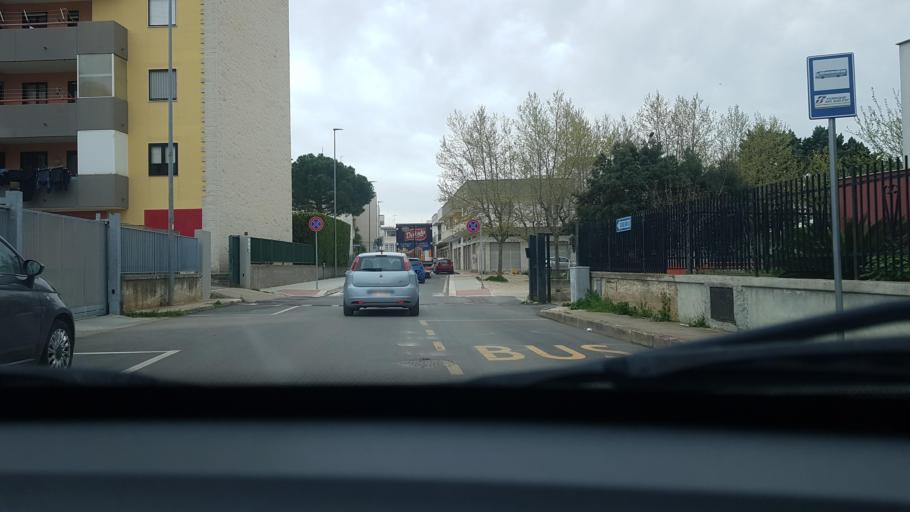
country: IT
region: Apulia
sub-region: Provincia di Bari
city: Noicattaro
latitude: 41.0340
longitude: 16.9829
